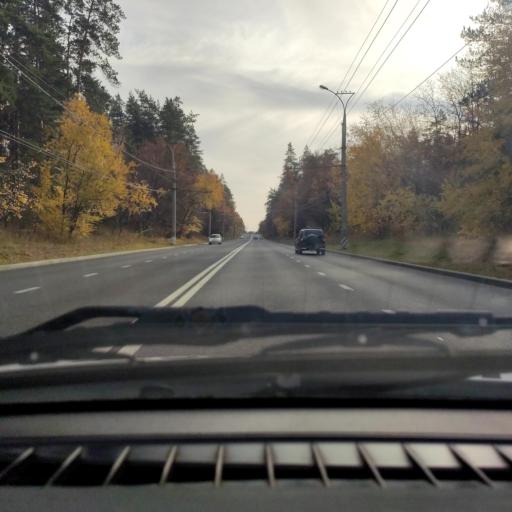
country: RU
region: Samara
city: Zhigulevsk
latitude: 53.4992
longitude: 49.4633
